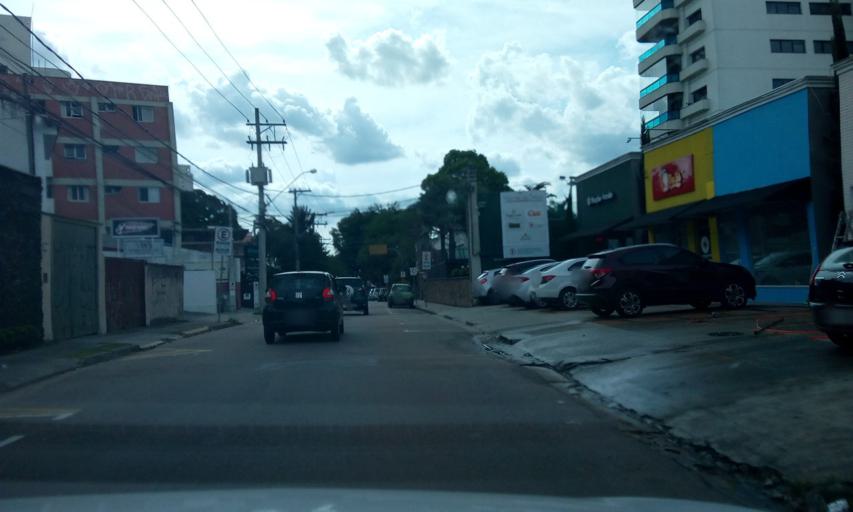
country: BR
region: Sao Paulo
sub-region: Jundiai
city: Jundiai
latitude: -23.1885
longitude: -46.8935
